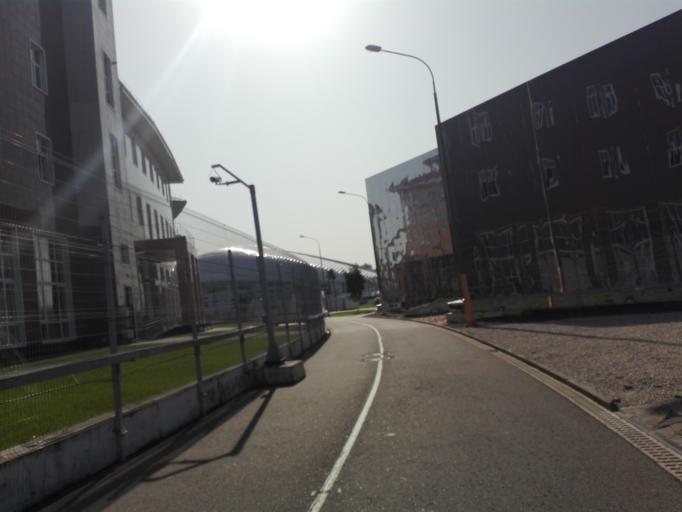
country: RU
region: Krasnodarskiy
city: Adler
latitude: 43.4054
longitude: 39.9616
